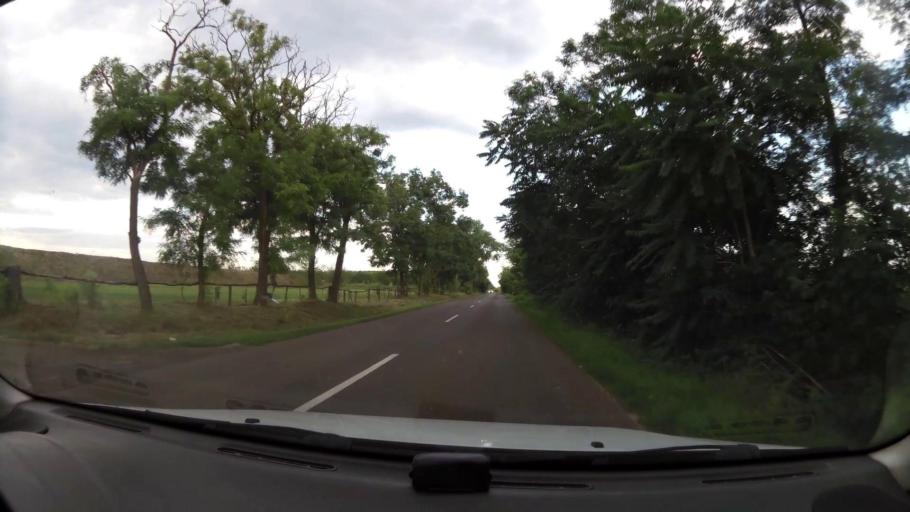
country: HU
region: Pest
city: Tapiosag
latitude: 47.3825
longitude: 19.6589
